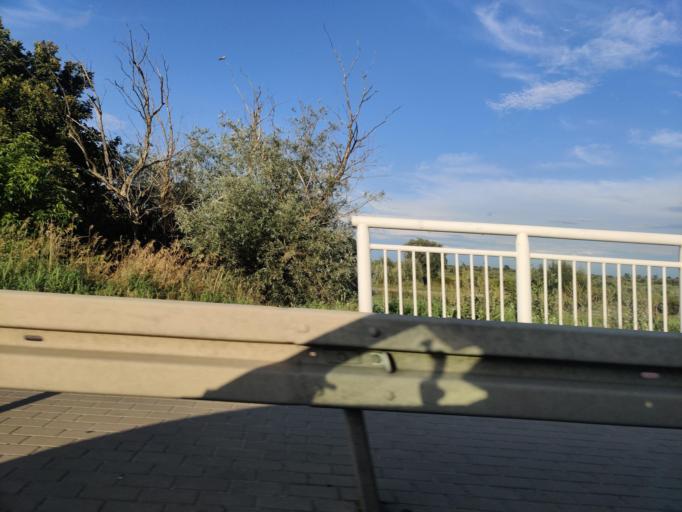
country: PL
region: Greater Poland Voivodeship
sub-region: Konin
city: Konin
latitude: 52.2214
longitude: 18.2518
